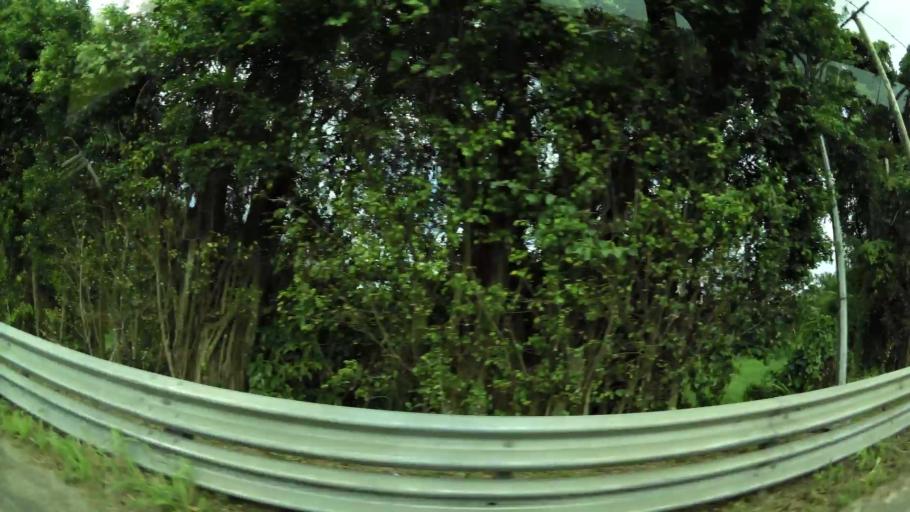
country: GP
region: Guadeloupe
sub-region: Guadeloupe
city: Pointe-a-Pitre
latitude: 16.2549
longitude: -61.5528
